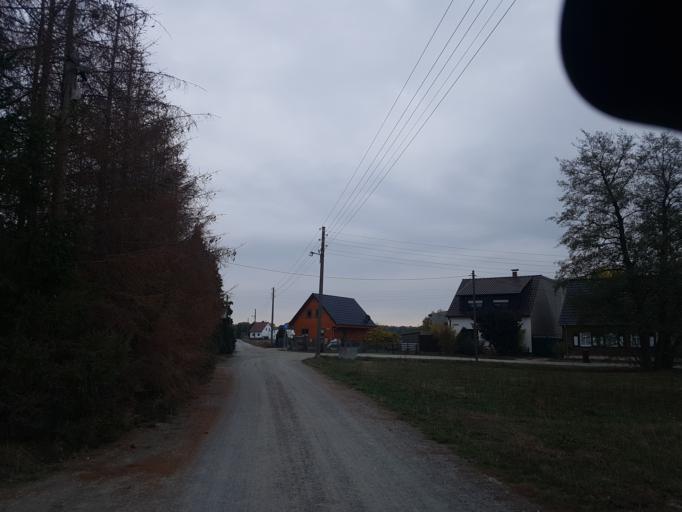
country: DE
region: Brandenburg
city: Finsterwalde
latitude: 51.6118
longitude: 13.7193
